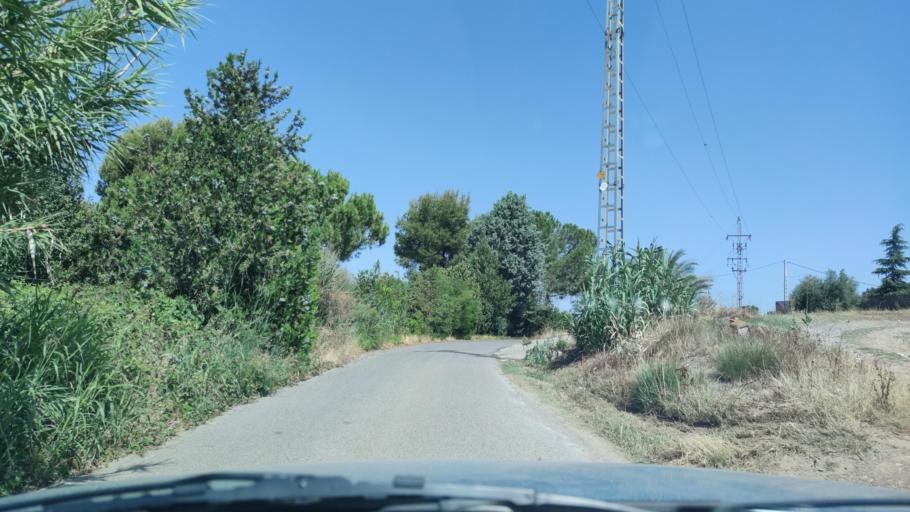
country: ES
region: Catalonia
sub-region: Provincia de Lleida
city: Torrefarrera
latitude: 41.6391
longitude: 0.5899
